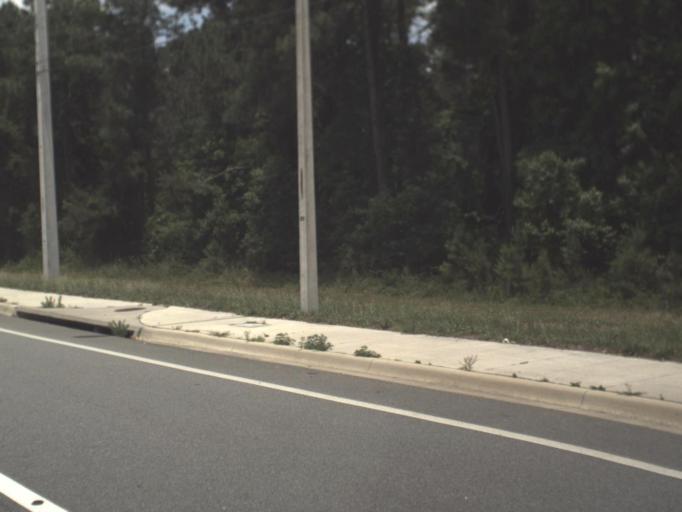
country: US
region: Florida
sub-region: Duval County
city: Atlantic Beach
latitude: 30.3220
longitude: -81.4984
